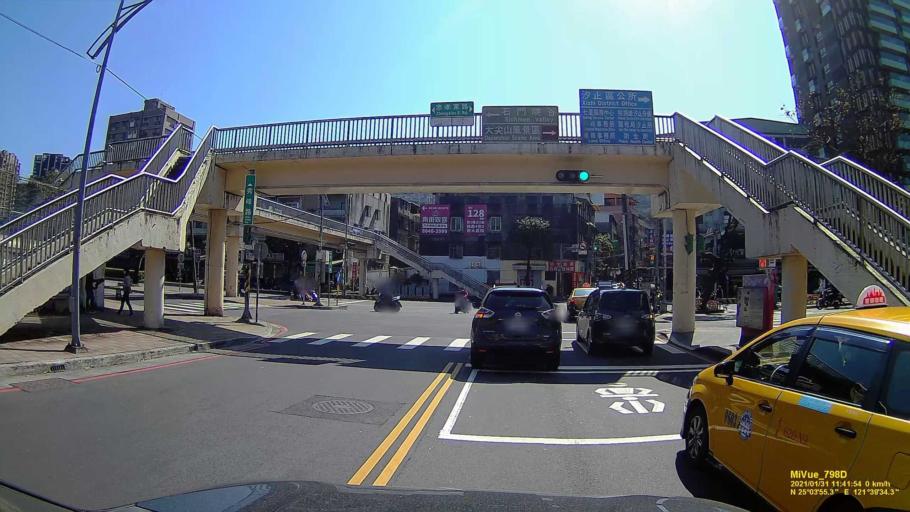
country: TW
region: Taiwan
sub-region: Keelung
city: Keelung
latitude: 25.0651
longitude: 121.6594
